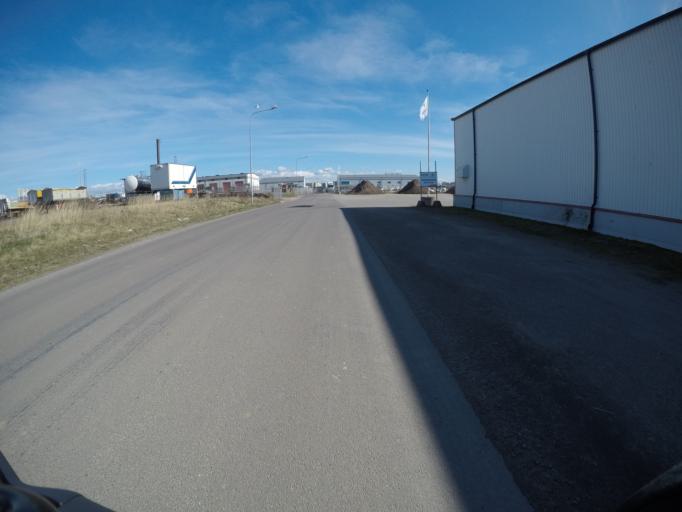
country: SE
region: Halland
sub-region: Laholms Kommun
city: Laholm
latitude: 56.4990
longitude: 13.0133
